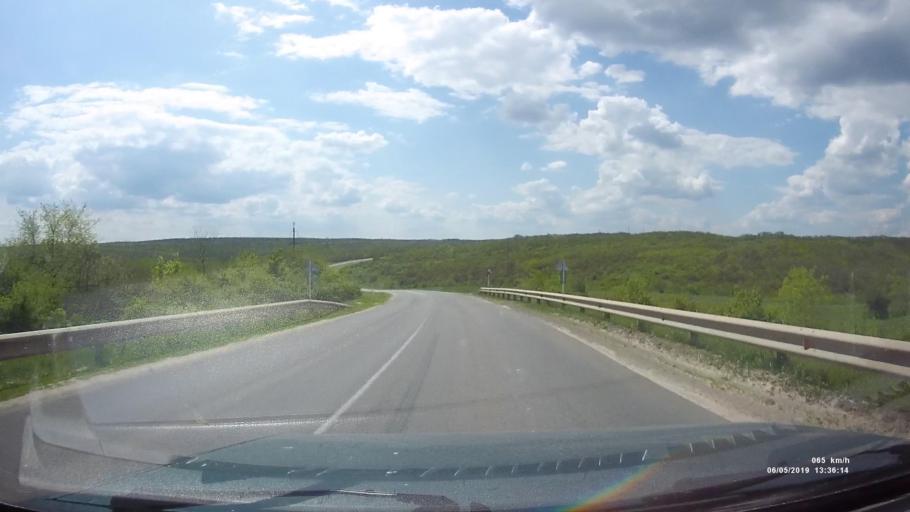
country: RU
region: Rostov
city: Ust'-Donetskiy
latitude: 47.6918
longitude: 40.7349
